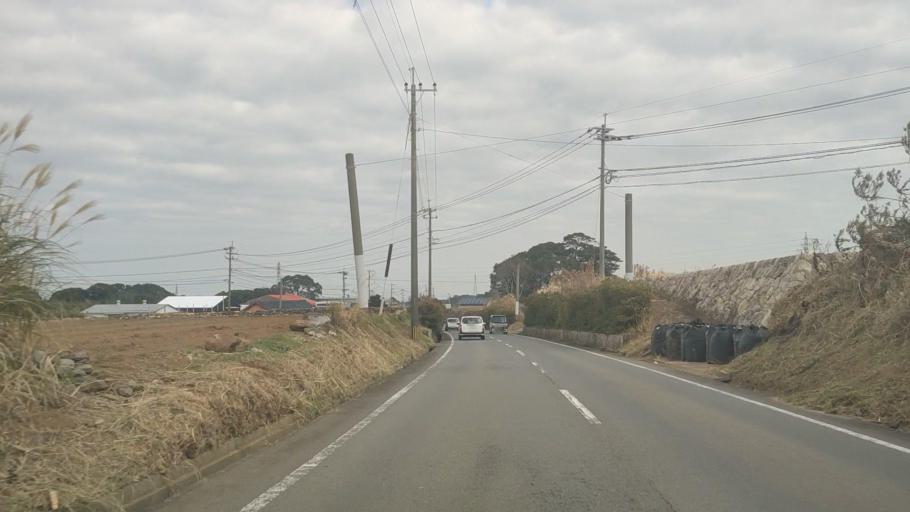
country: JP
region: Nagasaki
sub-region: Isahaya-shi
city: Isahaya
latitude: 32.8006
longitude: 130.1655
